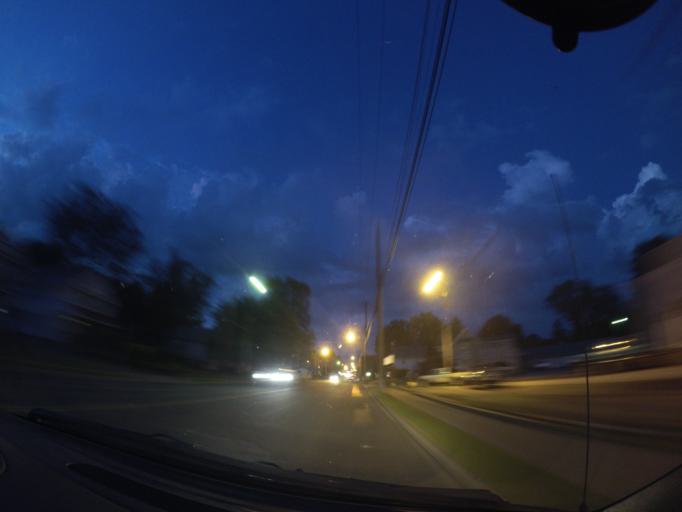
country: US
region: Ohio
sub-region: Ashtabula County
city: Ashtabula
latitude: 41.8603
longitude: -80.8035
